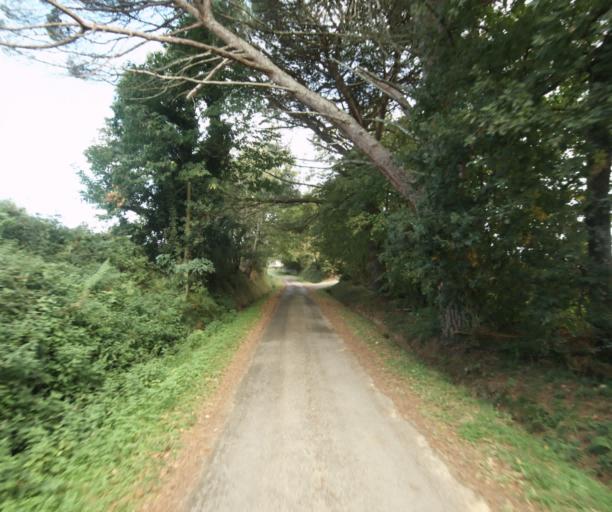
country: FR
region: Aquitaine
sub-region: Departement des Landes
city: Villeneuve-de-Marsan
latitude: 43.9146
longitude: -0.2166
